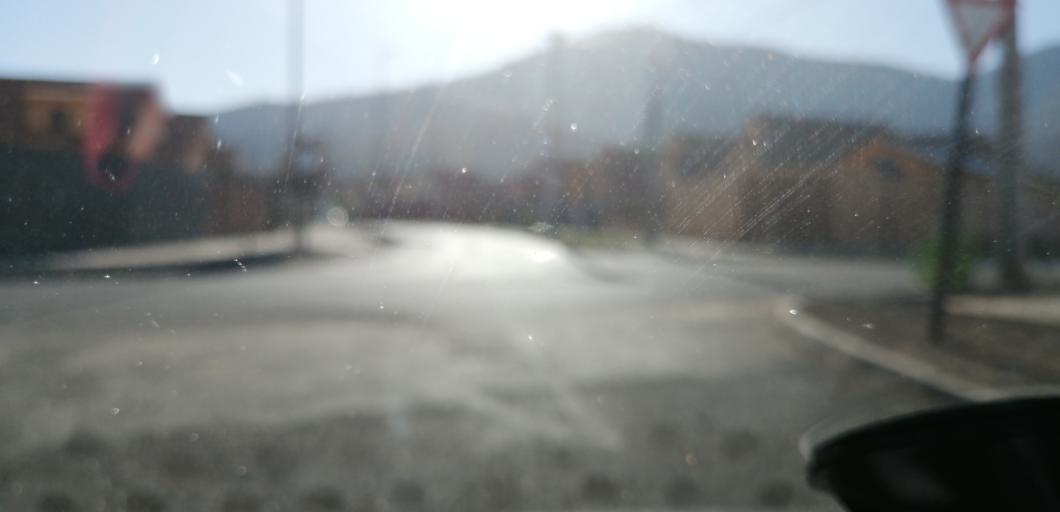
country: CL
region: Santiago Metropolitan
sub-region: Provincia de Santiago
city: Lo Prado
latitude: -33.4652
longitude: -70.8564
